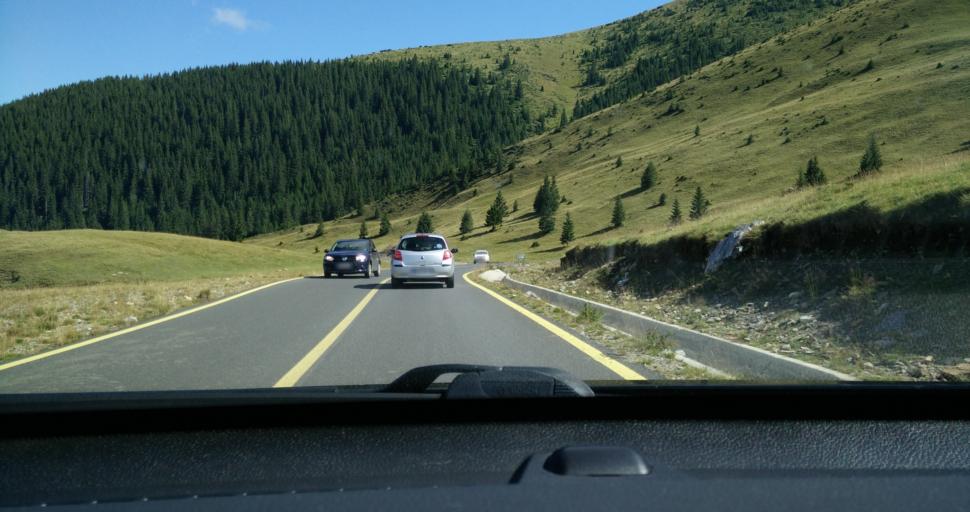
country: RO
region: Gorj
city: Novaci-Straini
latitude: 45.3877
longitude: 23.6434
